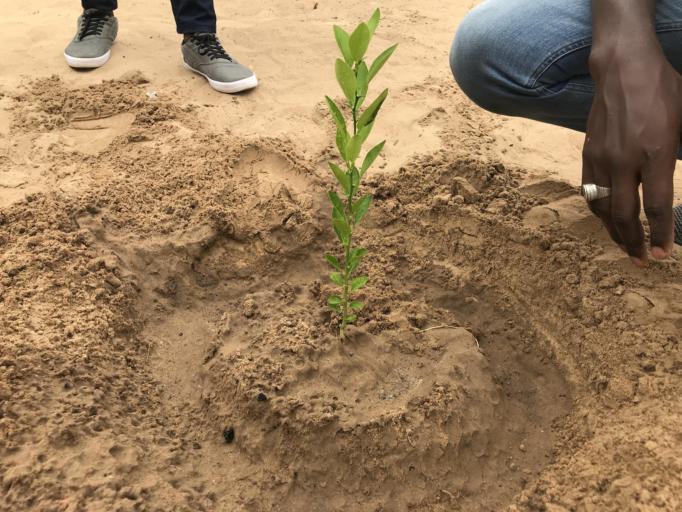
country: SN
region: Saint-Louis
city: Saint-Louis
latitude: 15.9329
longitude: -16.4687
